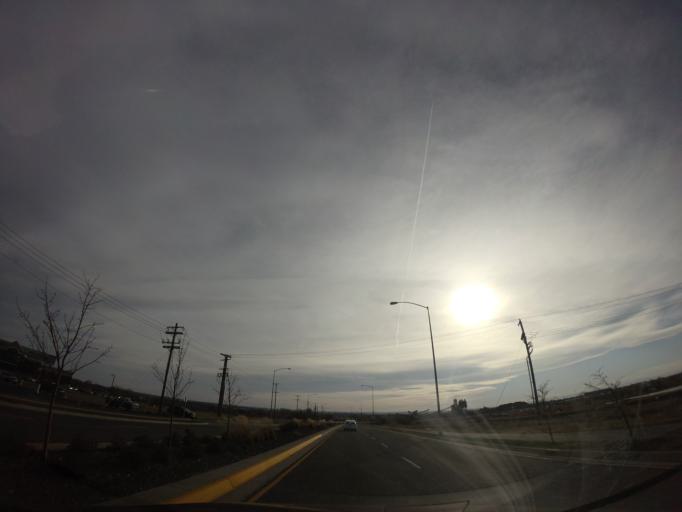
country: US
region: Montana
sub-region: Yellowstone County
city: Billings
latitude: 45.7497
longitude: -108.6176
